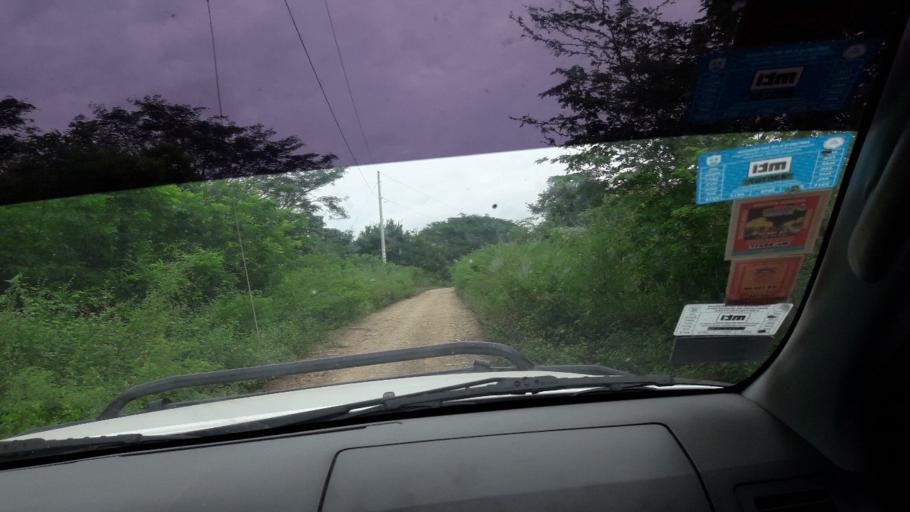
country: NI
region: Rivas
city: San Juan del Sur
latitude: 11.1974
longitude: -85.7684
